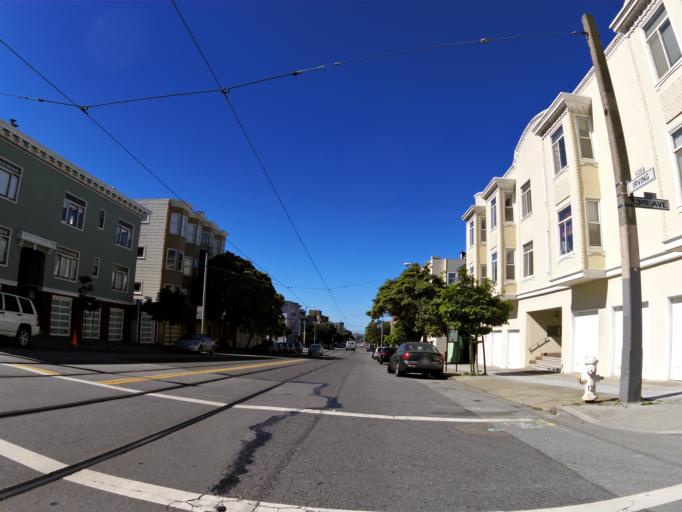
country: US
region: California
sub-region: San Francisco County
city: San Francisco
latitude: 37.7644
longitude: -122.4599
